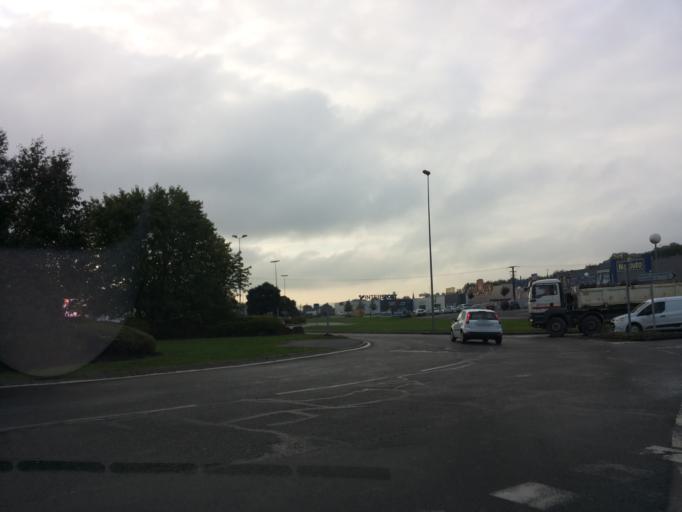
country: FR
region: Champagne-Ardenne
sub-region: Departement des Ardennes
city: Villers-Semeuse
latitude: 49.7327
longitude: 4.7518
